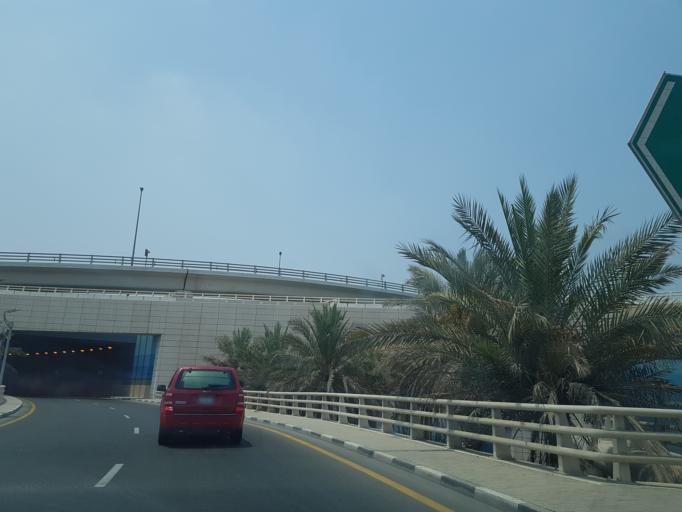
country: AE
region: Ash Shariqah
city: Sharjah
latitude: 25.2462
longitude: 55.3569
